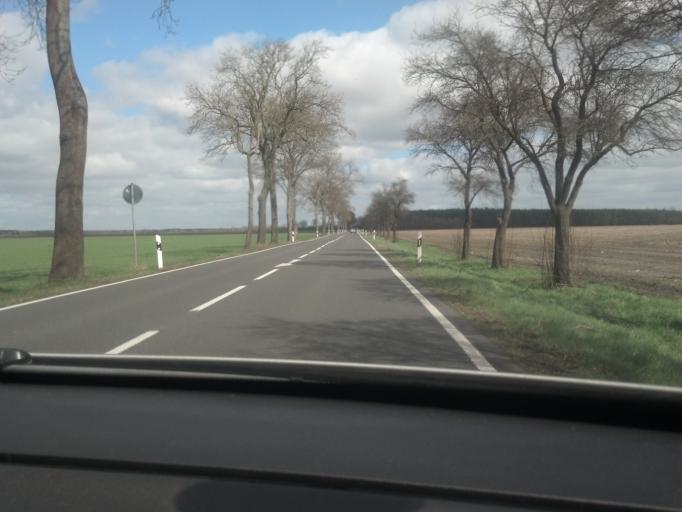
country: DE
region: Brandenburg
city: Gerdshagen
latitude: 53.3243
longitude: 12.2401
